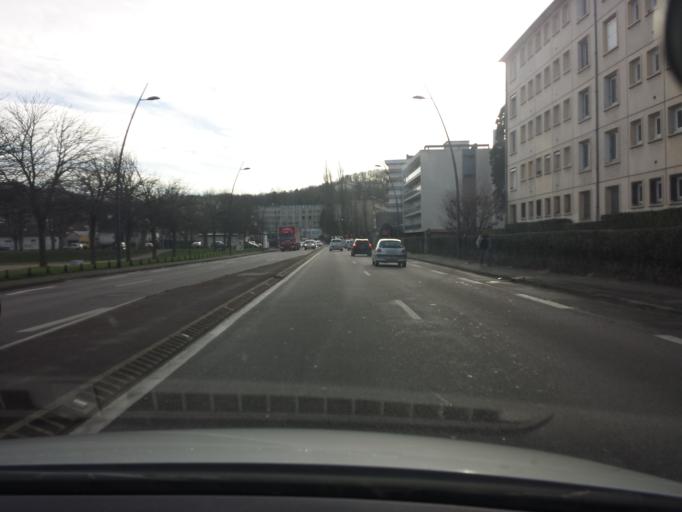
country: FR
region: Haute-Normandie
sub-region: Departement de l'Eure
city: Evreux
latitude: 49.0208
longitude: 1.1380
